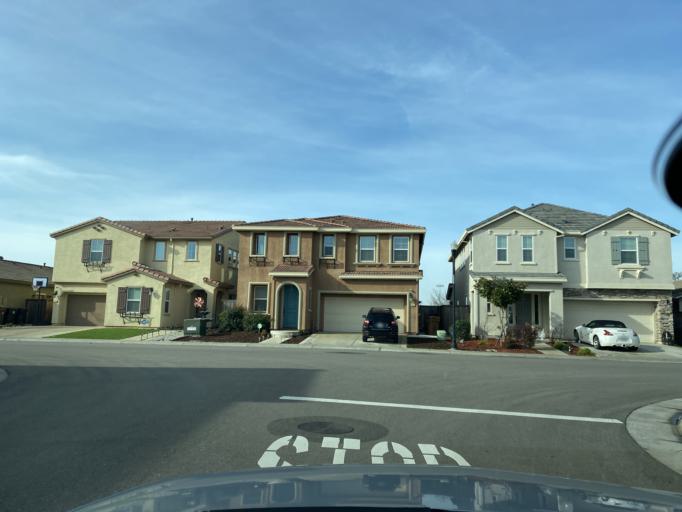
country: US
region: California
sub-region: Sacramento County
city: Elk Grove
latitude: 38.4004
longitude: -121.3937
